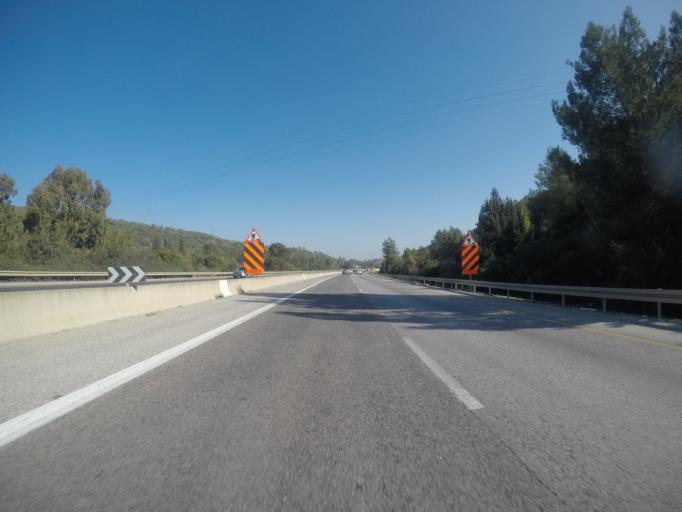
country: IL
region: Haifa
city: Daliyat el Karmil
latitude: 32.6500
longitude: 35.0854
